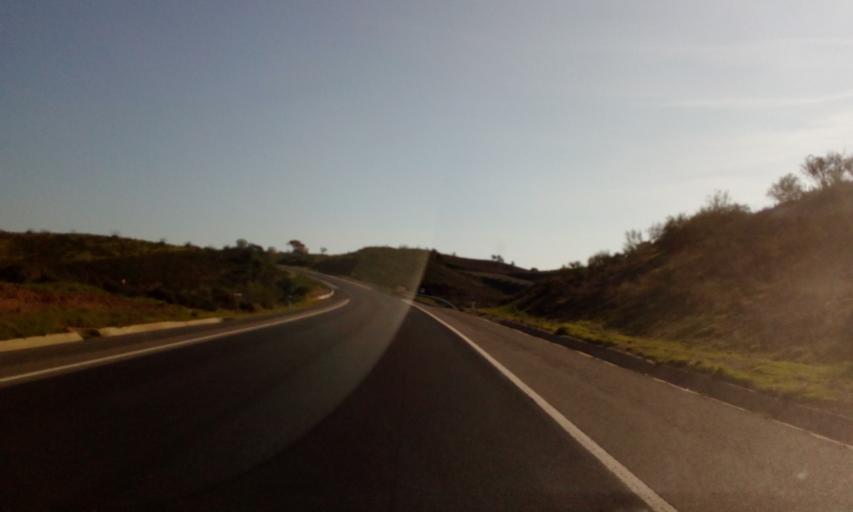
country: PT
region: Faro
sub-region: Castro Marim
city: Castro Marim
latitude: 37.2468
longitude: -7.4700
